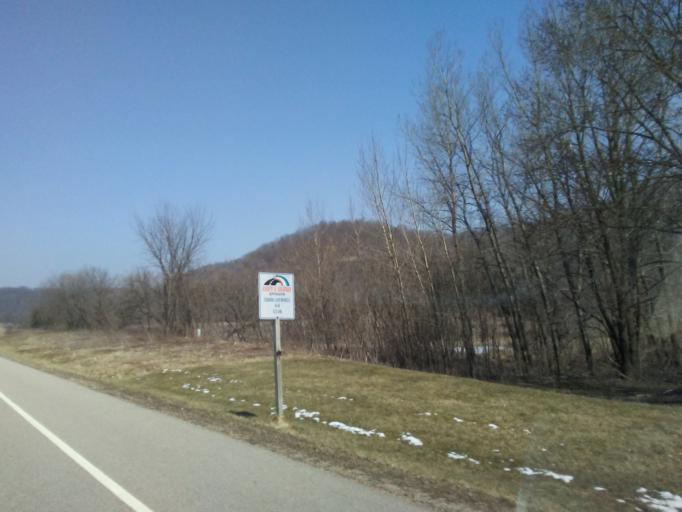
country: US
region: Wisconsin
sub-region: Richland County
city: Richland Center
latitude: 43.3594
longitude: -90.5576
